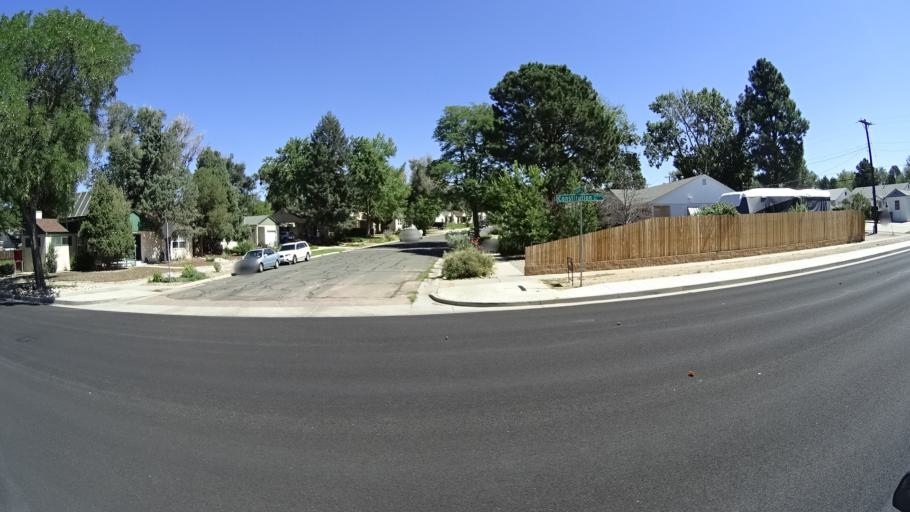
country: US
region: Colorado
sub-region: El Paso County
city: Colorado Springs
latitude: 38.8647
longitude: -104.8009
